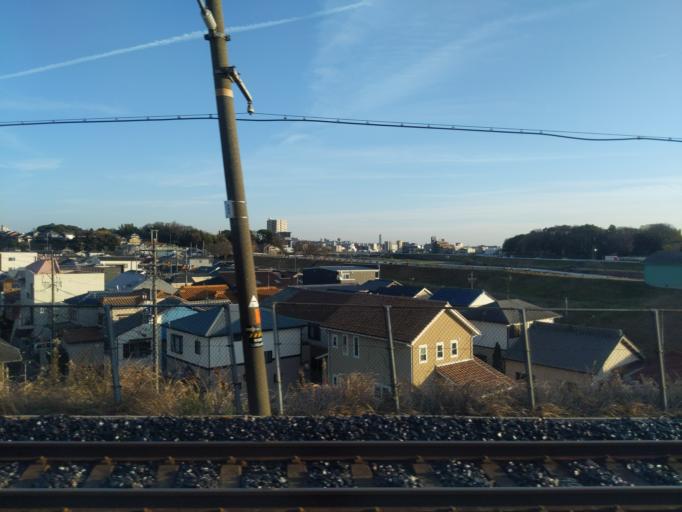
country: JP
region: Aichi
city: Nagoya-shi
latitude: 35.2000
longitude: 136.9451
